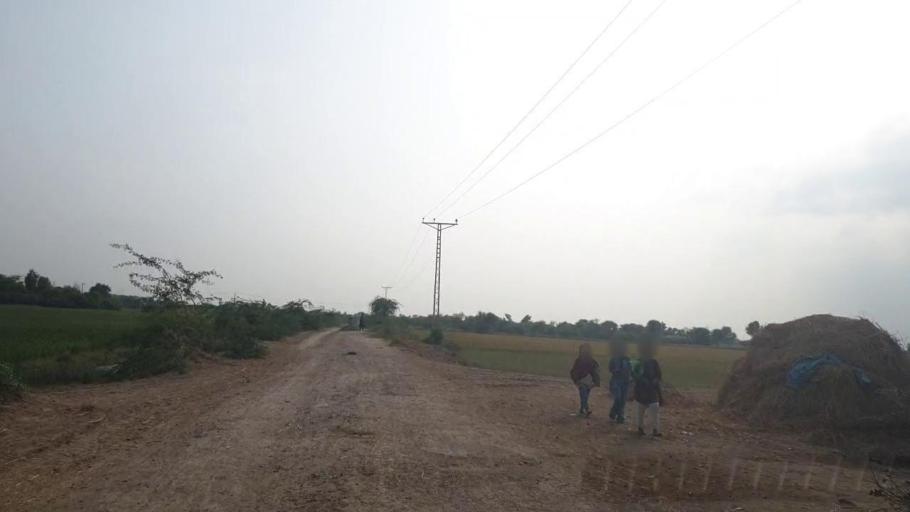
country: PK
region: Sindh
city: Badin
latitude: 24.6206
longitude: 68.6879
